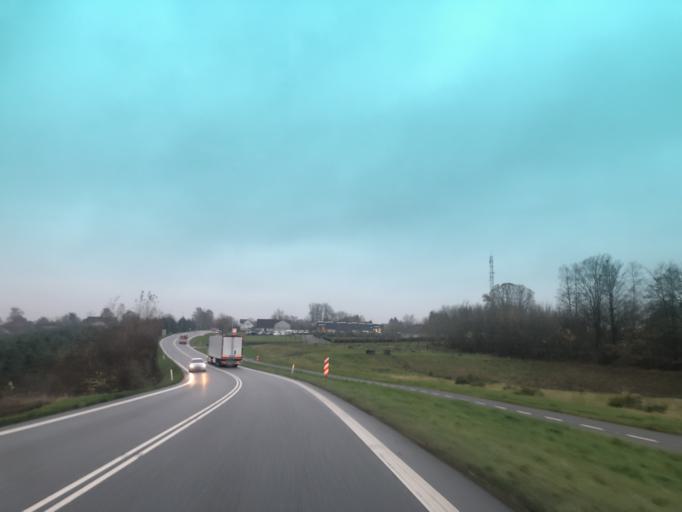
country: DK
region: South Denmark
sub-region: Nyborg Kommune
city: Ullerslev
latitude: 55.2669
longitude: 10.6753
